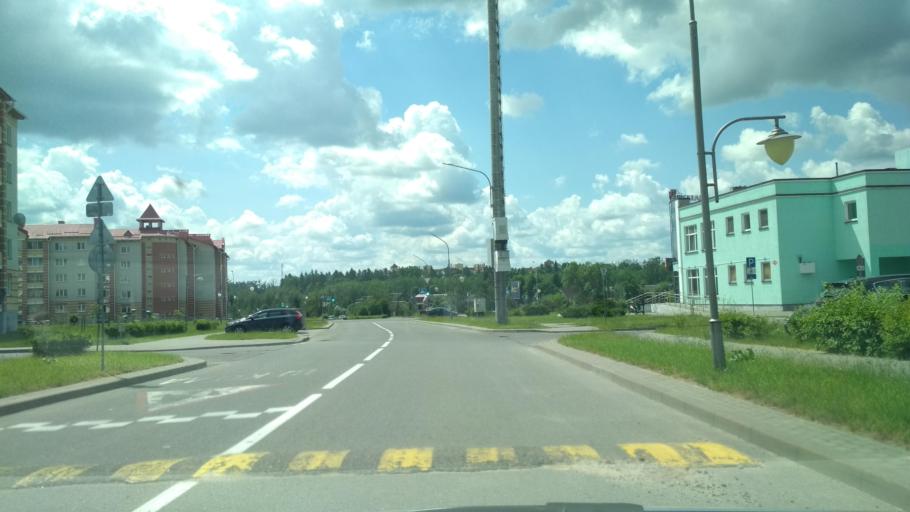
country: BY
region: Grodnenskaya
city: Astravyets
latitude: 54.6156
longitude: 25.9760
